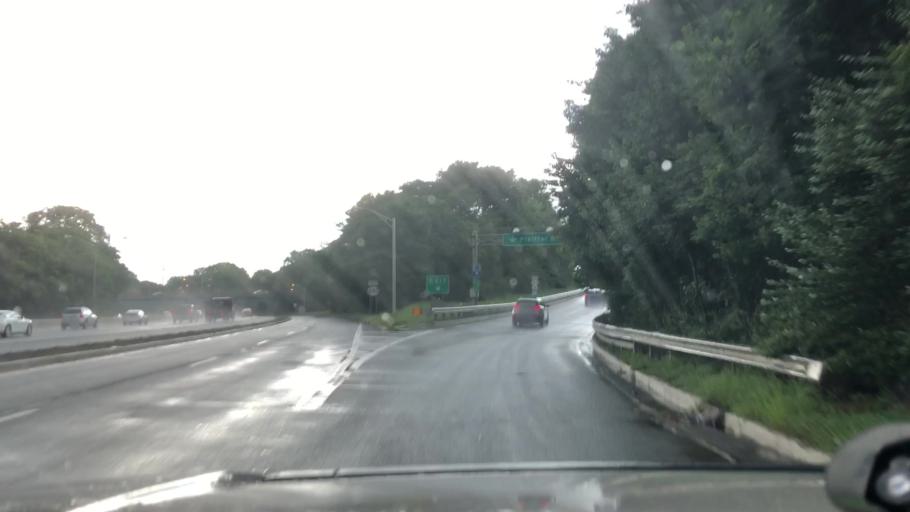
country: US
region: New Jersey
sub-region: Middlesex County
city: Perth Amboy
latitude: 40.5294
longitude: -74.2801
